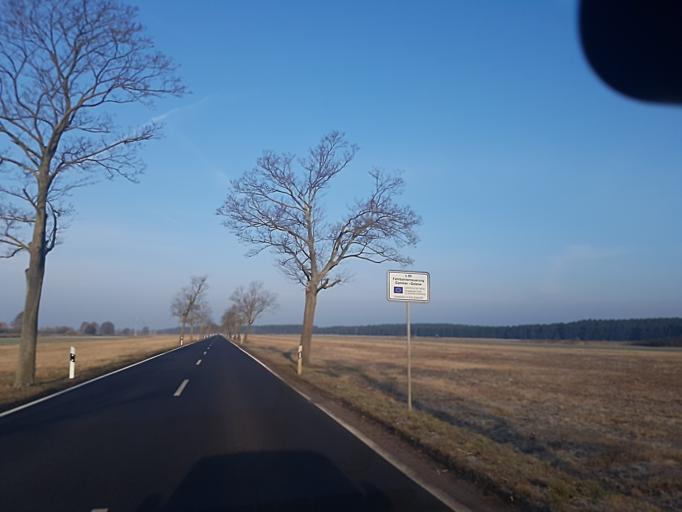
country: DE
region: Brandenburg
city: Golzow
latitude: 52.2628
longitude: 12.6592
